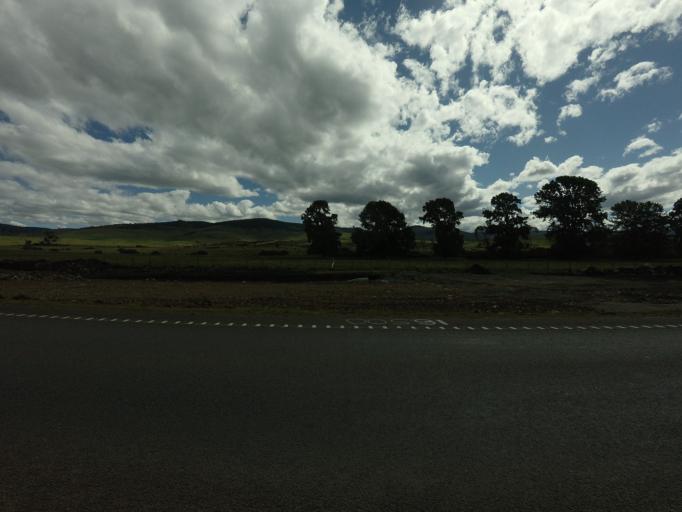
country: AU
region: Tasmania
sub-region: Brighton
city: Bridgewater
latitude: -42.1920
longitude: 147.3902
